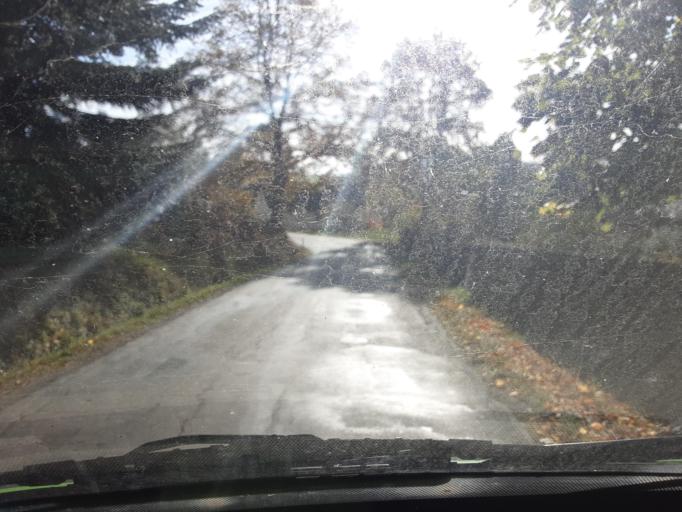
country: CZ
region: Plzensky
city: Janovice nad Uhlavou
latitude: 49.3813
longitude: 13.1682
